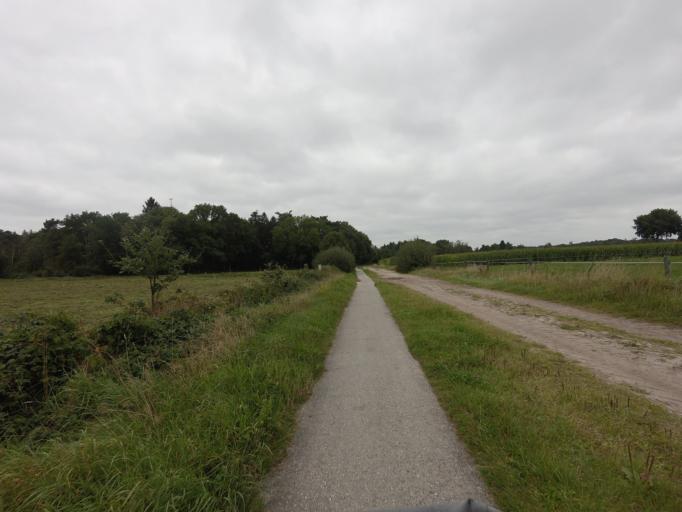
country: NL
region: Overijssel
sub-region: Gemeente Steenwijkerland
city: Steenwijk
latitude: 52.8080
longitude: 6.1192
